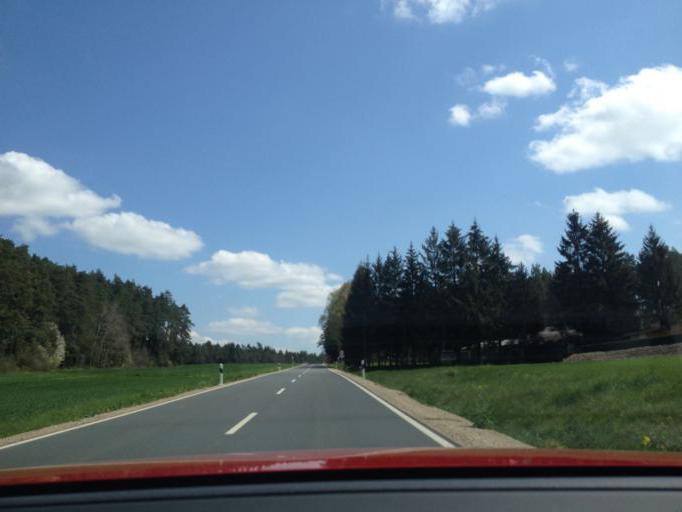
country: DE
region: Bavaria
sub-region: Upper Franconia
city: Pegnitz
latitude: 49.7291
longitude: 11.4742
